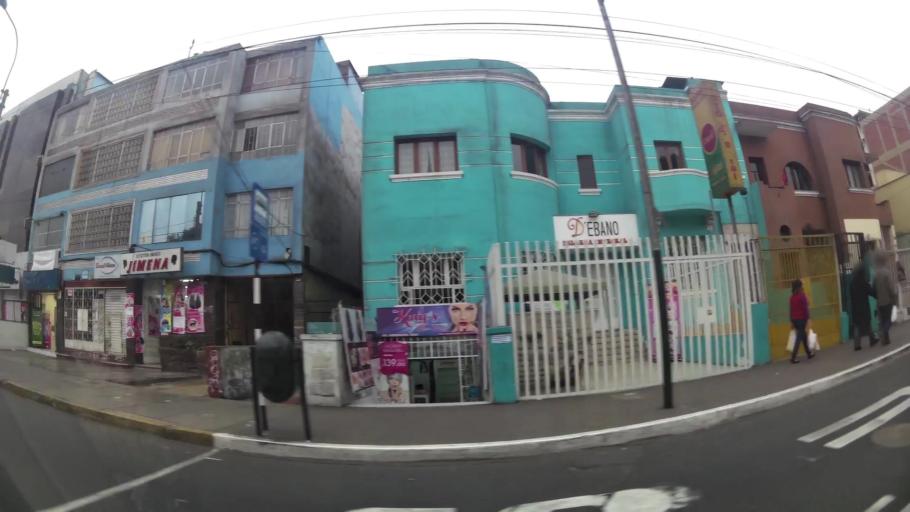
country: PE
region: Lima
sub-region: Lima
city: San Isidro
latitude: -12.0851
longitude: -77.0344
